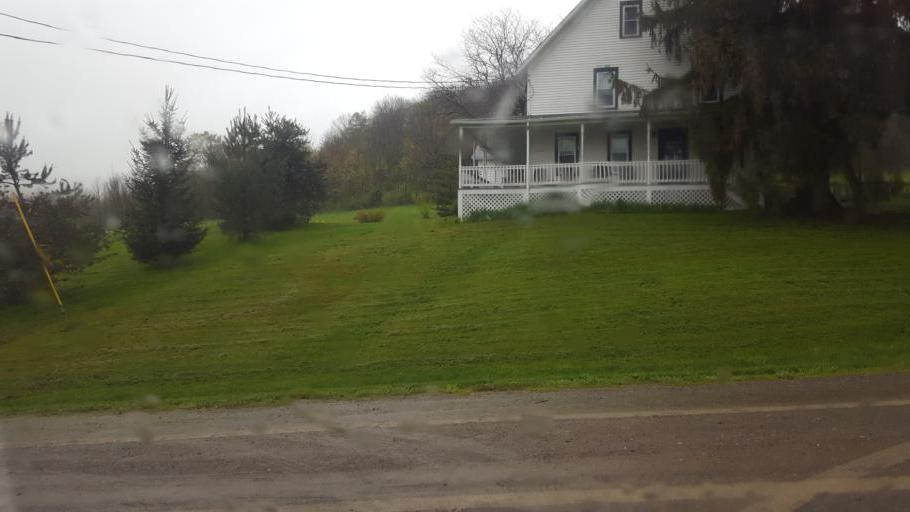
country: US
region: Pennsylvania
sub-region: Tioga County
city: Westfield
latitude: 42.0612
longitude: -77.4820
